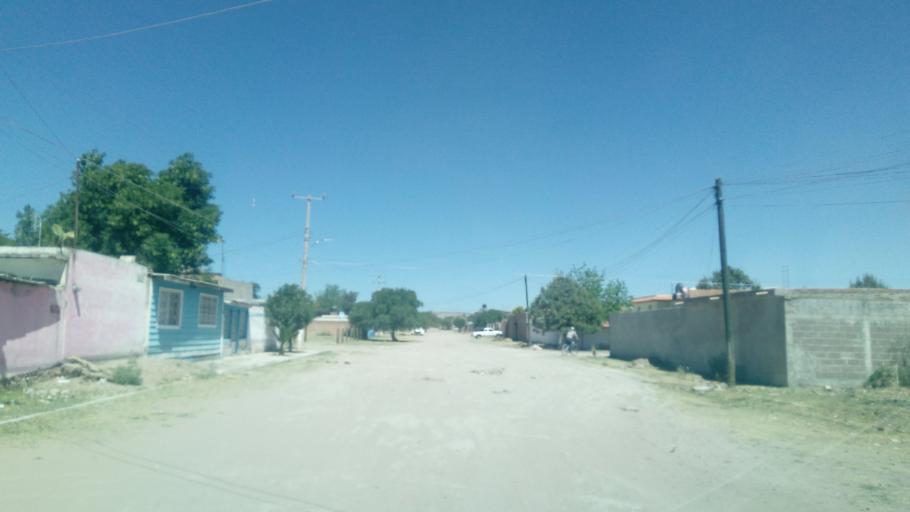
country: MX
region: Durango
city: Victoria de Durango
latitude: 24.0777
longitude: -104.6583
